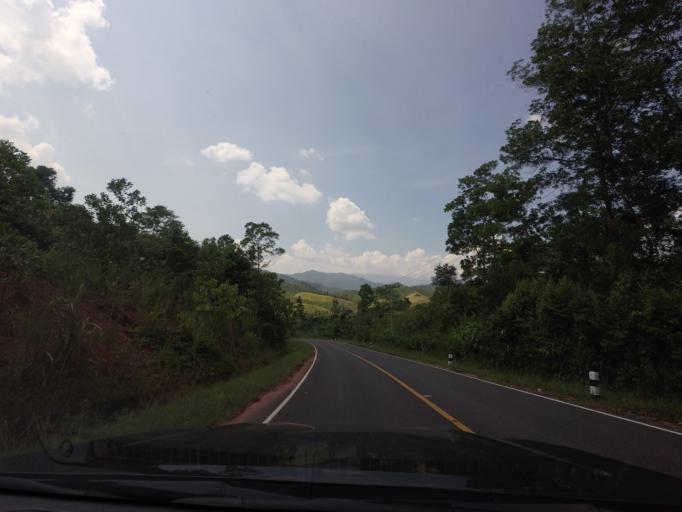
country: TH
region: Nan
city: Bo Kluea
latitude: 19.0118
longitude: 101.1951
